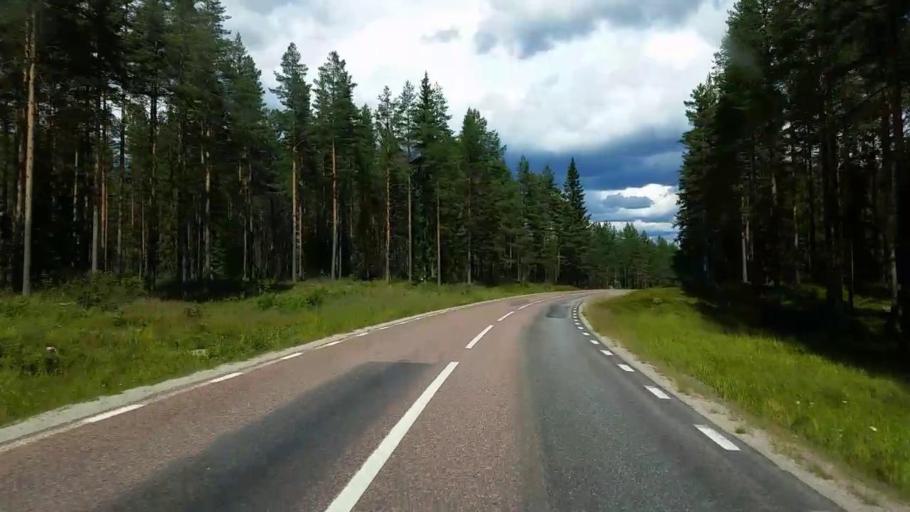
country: SE
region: Gaevleborg
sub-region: Ovanakers Kommun
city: Edsbyn
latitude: 61.3206
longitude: 15.5125
